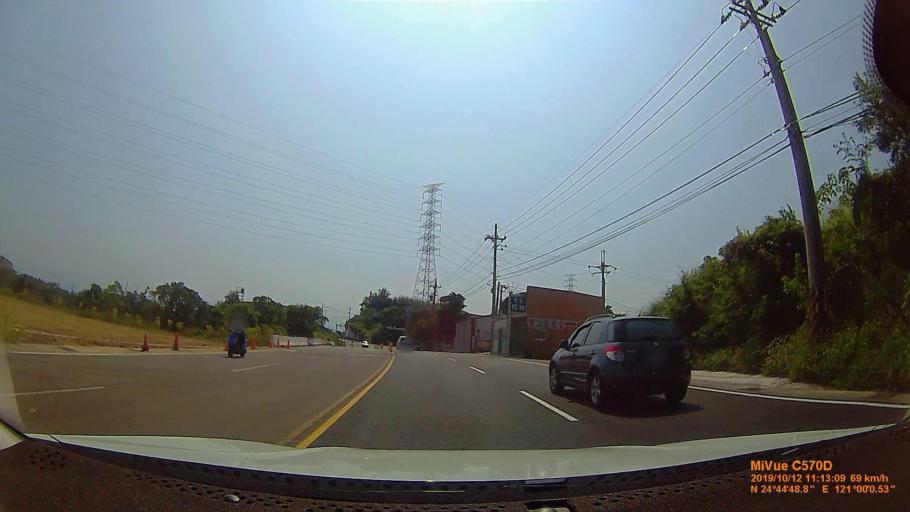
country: TW
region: Taiwan
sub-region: Hsinchu
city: Hsinchu
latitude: 24.7467
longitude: 121.0002
